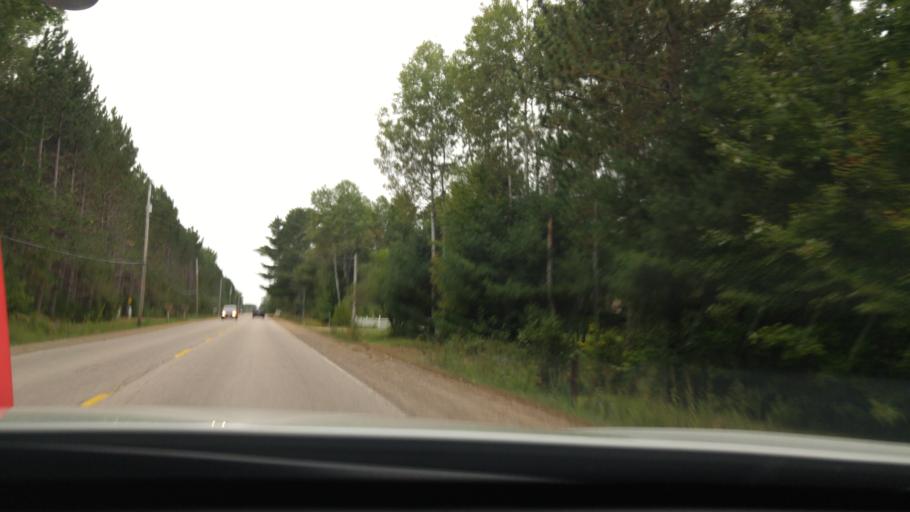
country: CA
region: Ontario
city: Petawawa
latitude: 45.8340
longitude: -77.2554
